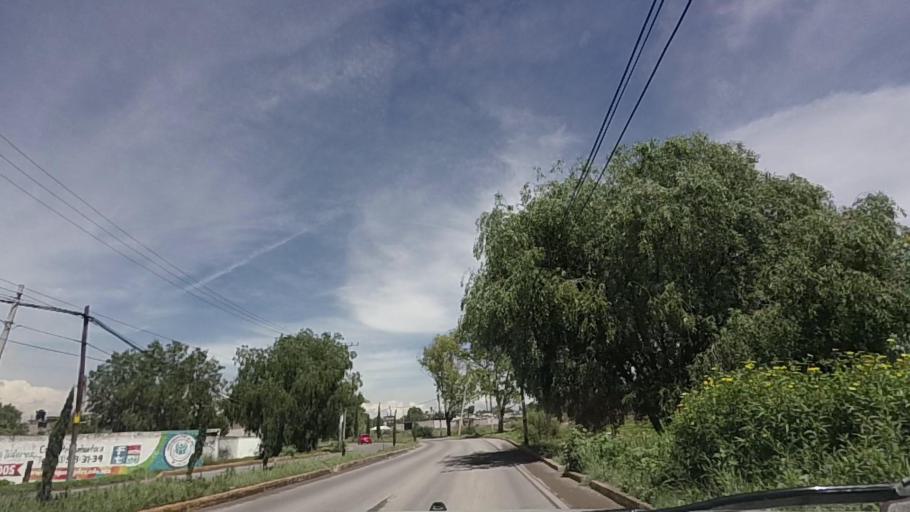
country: MX
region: Mexico
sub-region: Huehuetoca
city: Jorobas
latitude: 19.8261
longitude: -99.2421
